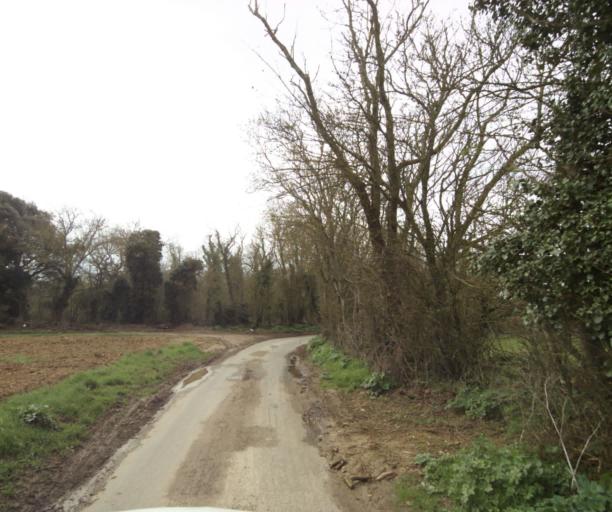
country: FR
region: Poitou-Charentes
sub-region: Departement de la Charente-Maritime
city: Nieul-sur-Mer
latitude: 46.1884
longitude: -1.1762
